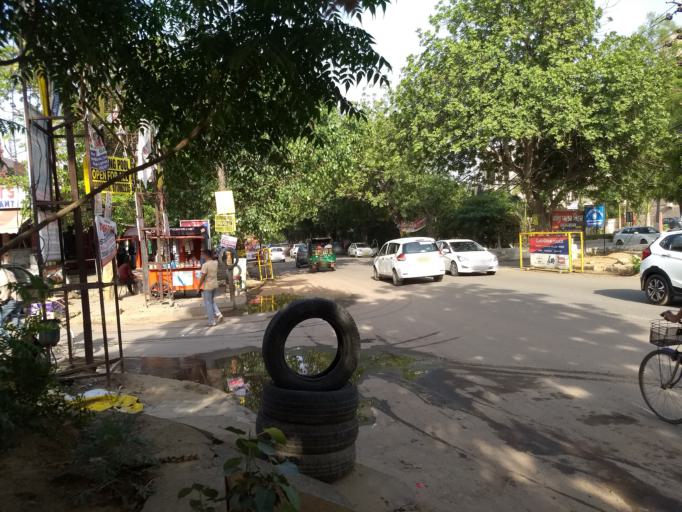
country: IN
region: Haryana
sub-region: Gurgaon
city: Gurgaon
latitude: 28.5027
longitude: 77.0628
